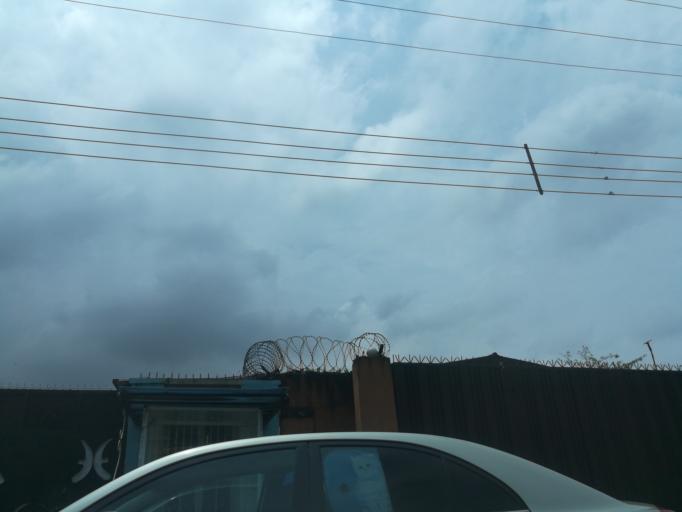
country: NG
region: Lagos
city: Ojota
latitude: 6.5902
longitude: 3.3624
